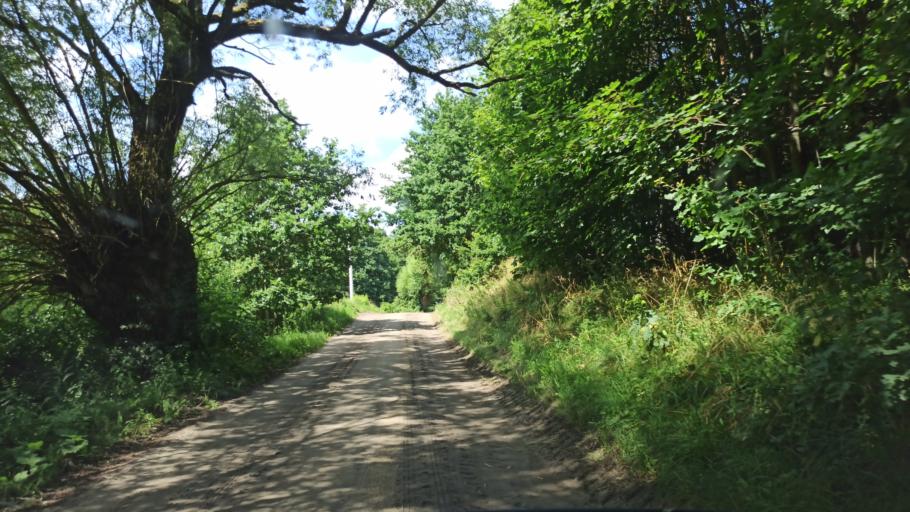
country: PL
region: Warmian-Masurian Voivodeship
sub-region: Powiat ostrodzki
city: Morag
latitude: 53.8635
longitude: 20.0581
